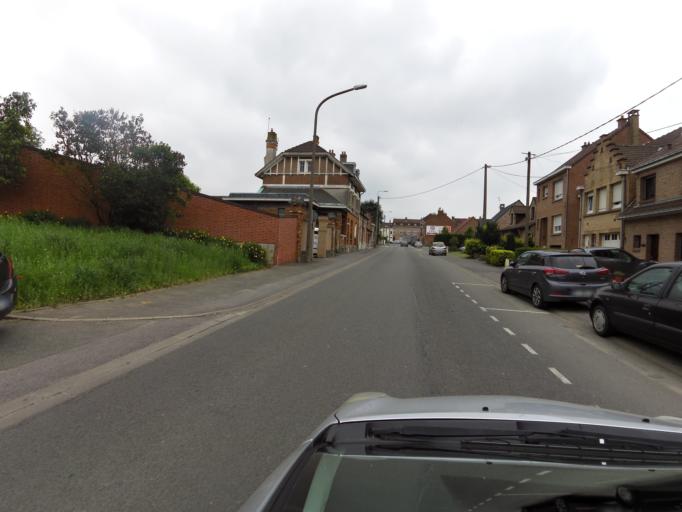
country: FR
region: Nord-Pas-de-Calais
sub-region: Departement du Nord
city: Bailleul
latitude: 50.7436
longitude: 2.7400
